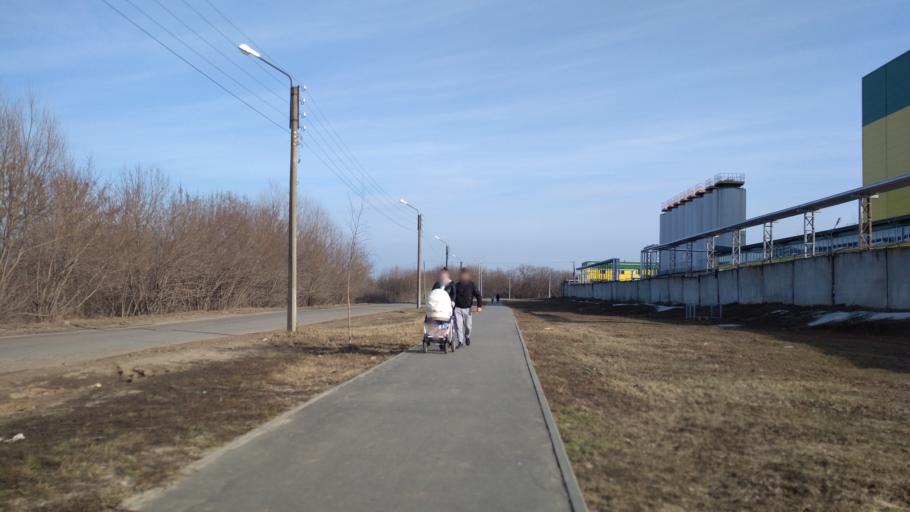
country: RU
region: Chuvashia
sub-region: Cheboksarskiy Rayon
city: Cheboksary
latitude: 56.1361
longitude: 47.3130
